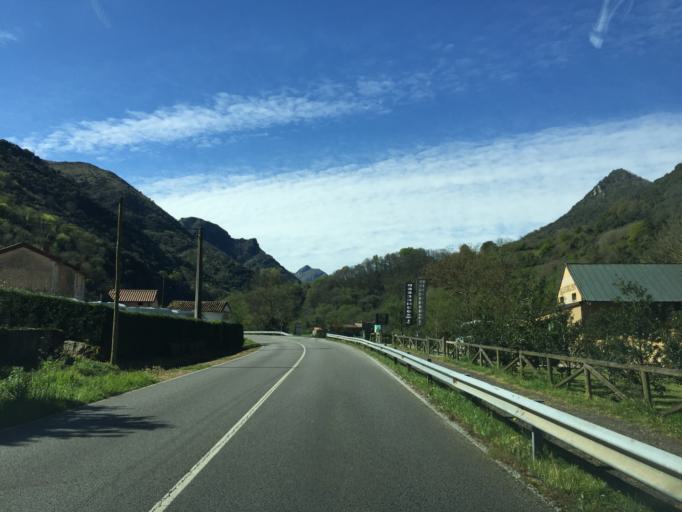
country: ES
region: Asturias
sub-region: Province of Asturias
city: Proaza
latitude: 43.2923
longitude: -5.9820
